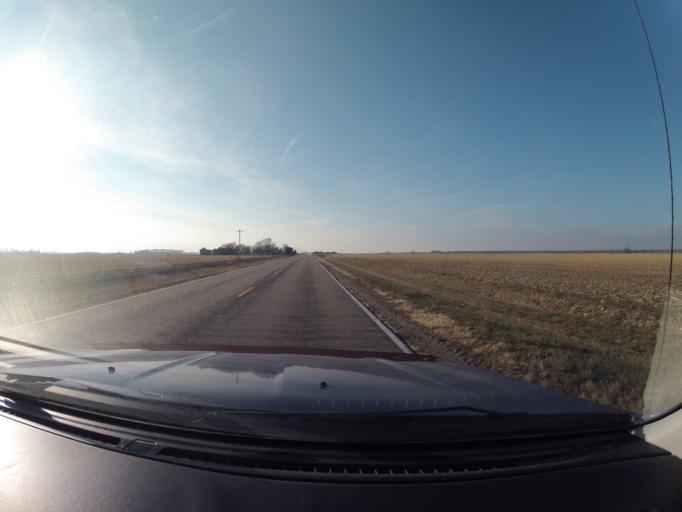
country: US
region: Nebraska
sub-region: Buffalo County
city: Kearney
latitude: 40.6410
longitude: -99.0383
